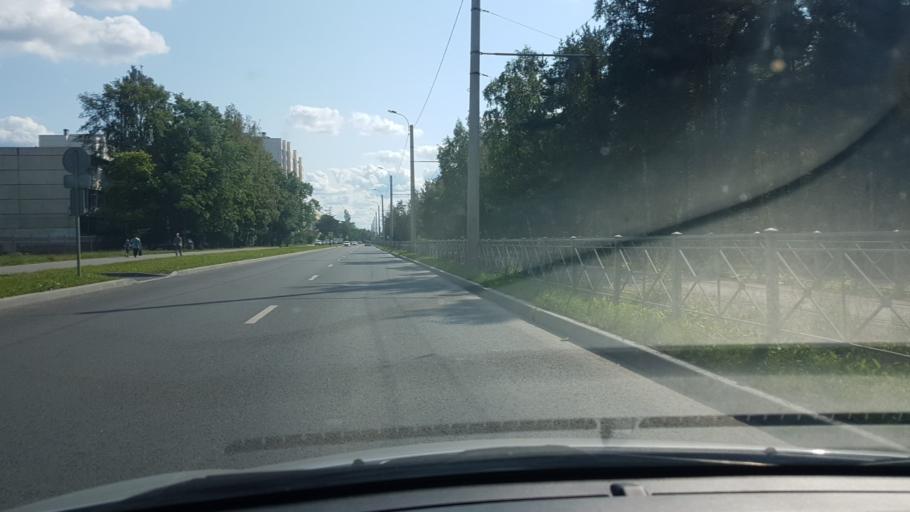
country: RU
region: St.-Petersburg
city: Sosnovaya Polyana
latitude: 59.8297
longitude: 30.1402
